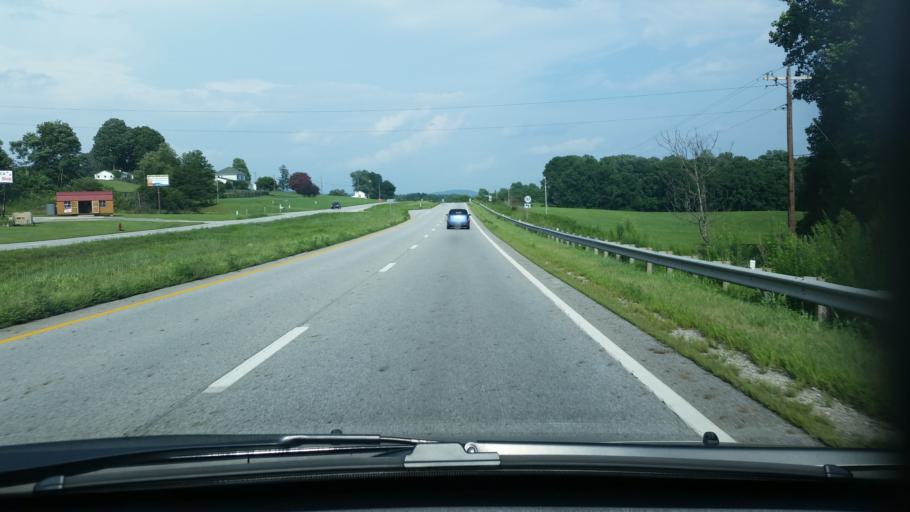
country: US
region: Virginia
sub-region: Nelson County
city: Lovingston
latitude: 37.7123
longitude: -78.9226
